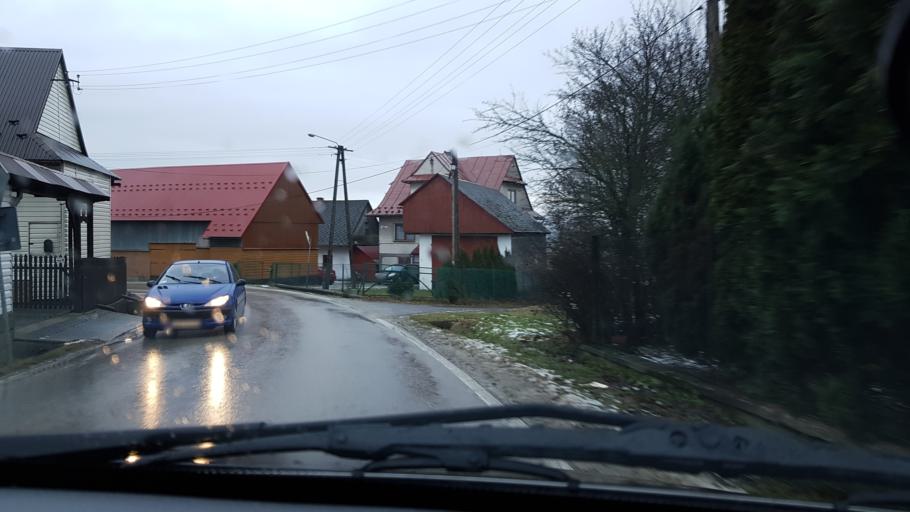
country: PL
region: Lesser Poland Voivodeship
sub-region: Powiat nowotarski
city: Sieniawa
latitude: 49.4885
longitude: 19.9040
